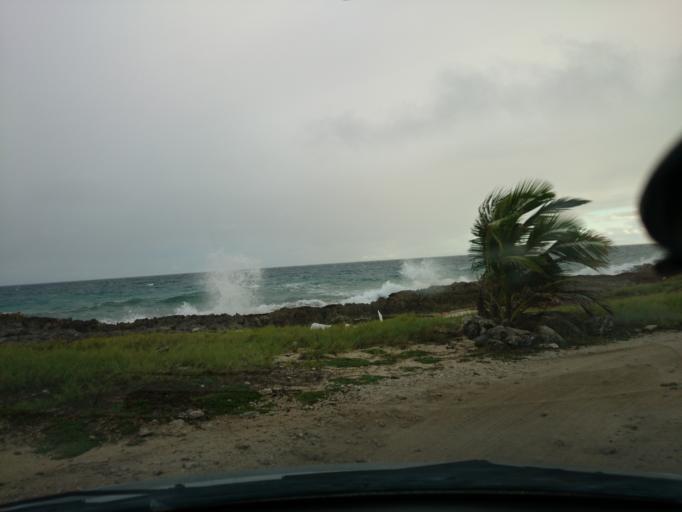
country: BB
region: Christ Church
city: Oistins
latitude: 13.0531
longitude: -59.5038
